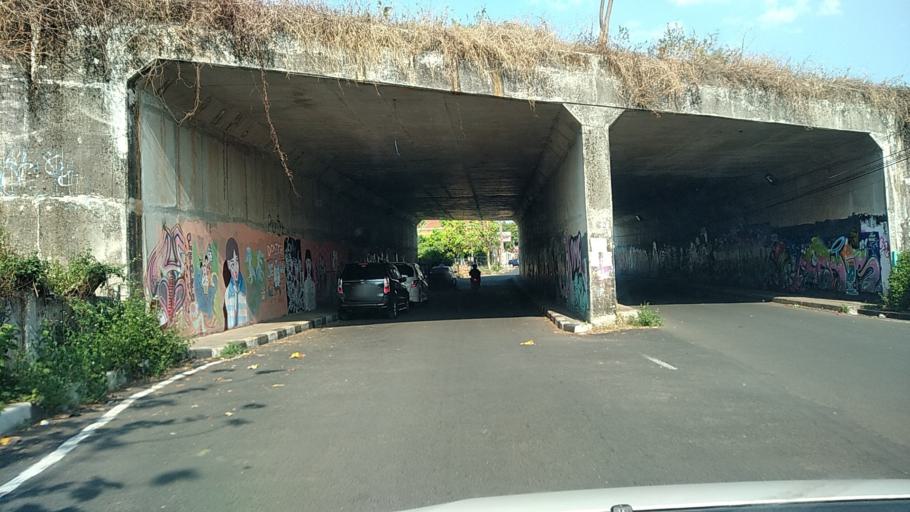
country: ID
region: Central Java
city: Semarang
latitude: -7.0579
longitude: 110.4238
